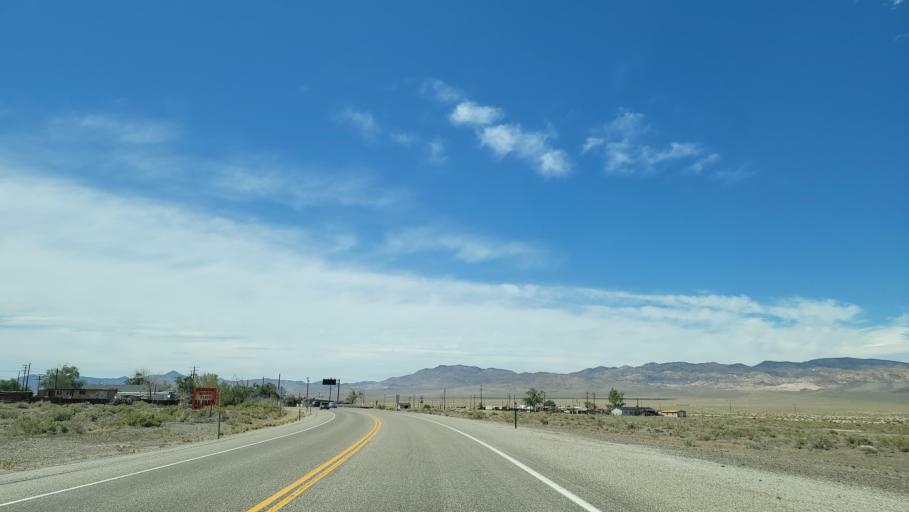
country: US
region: Nevada
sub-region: Mineral County
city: Hawthorne
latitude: 38.5028
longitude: -118.1755
